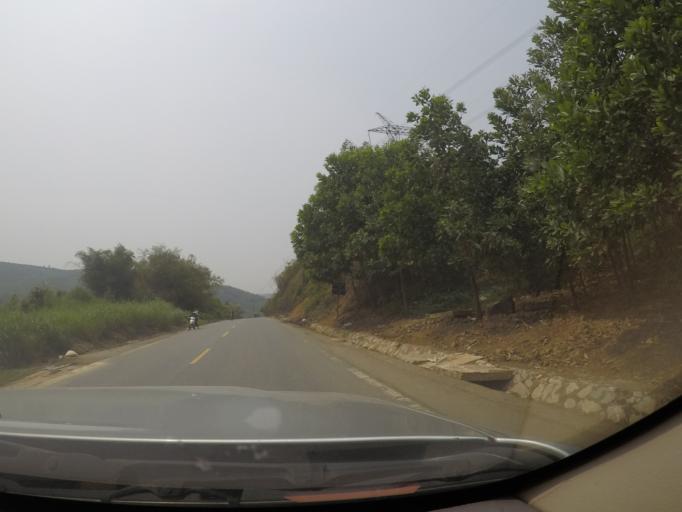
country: VN
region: Thanh Hoa
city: Thi Tran Cam Thuy
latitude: 20.1602
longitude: 105.4674
